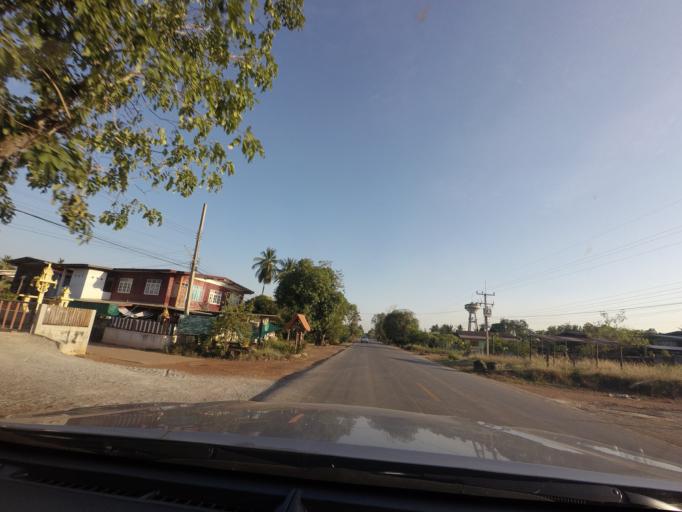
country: TH
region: Sukhothai
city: Sawankhalok
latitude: 17.3805
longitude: 99.7947
